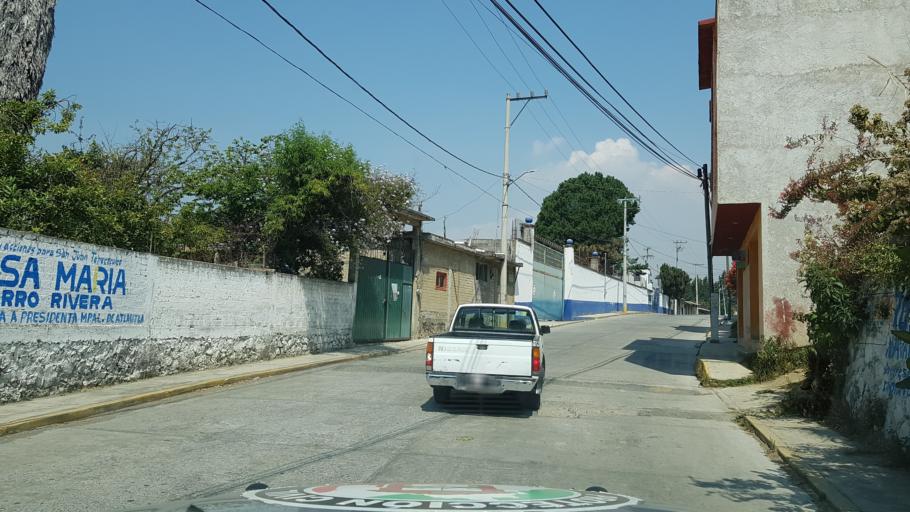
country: MX
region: Mexico
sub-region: Atlautla
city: San Juan Tepecoculco
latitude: 18.9863
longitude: -98.7896
